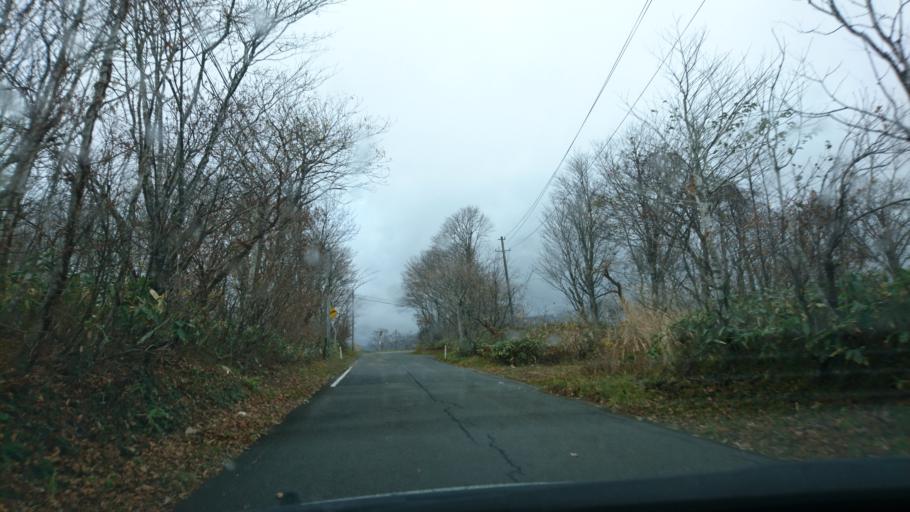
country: JP
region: Iwate
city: Ichinoseki
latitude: 38.9266
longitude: 140.8416
